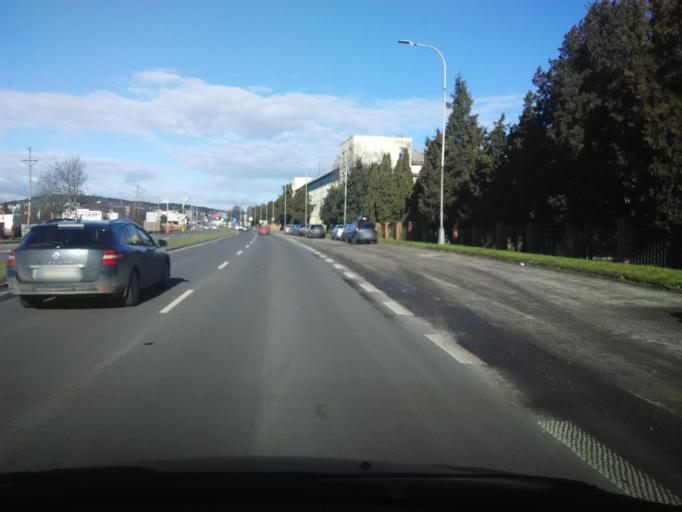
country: SK
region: Nitriansky
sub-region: Okres Nitra
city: Nitra
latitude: 48.2897
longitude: 18.0843
